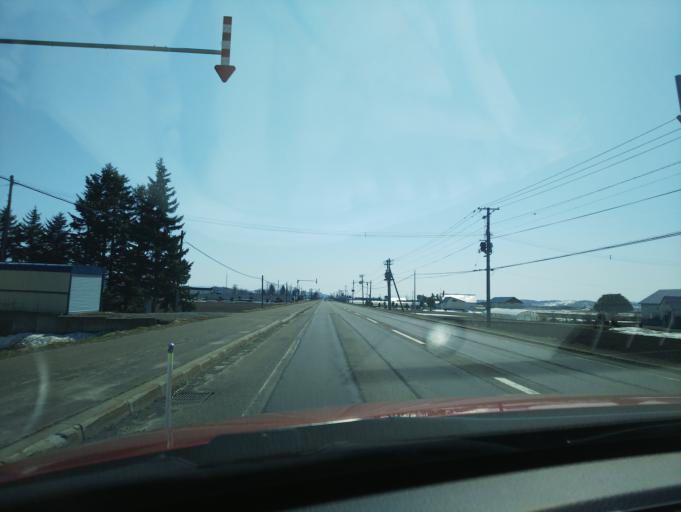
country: JP
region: Hokkaido
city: Nayoro
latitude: 44.2095
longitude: 142.3950
